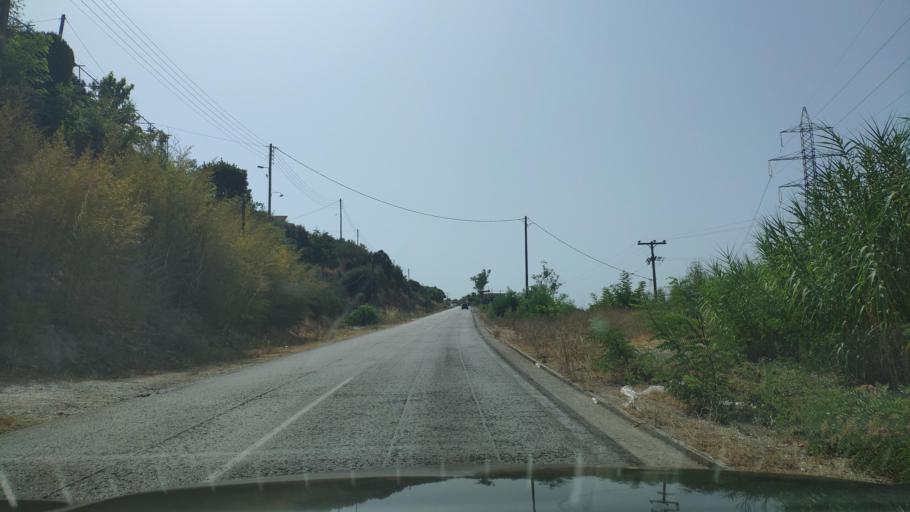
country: GR
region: Epirus
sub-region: Nomos Artas
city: Peta
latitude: 39.1596
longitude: 21.0239
